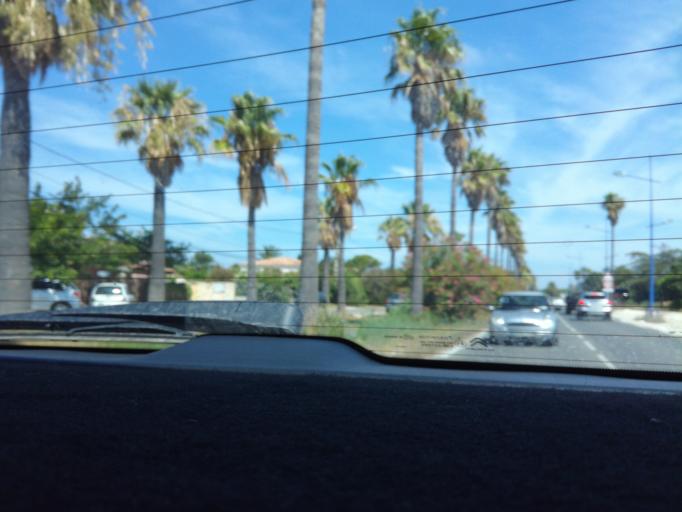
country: FR
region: Provence-Alpes-Cote d'Azur
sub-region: Departement du Var
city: Hyeres
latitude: 43.0456
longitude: 6.1461
